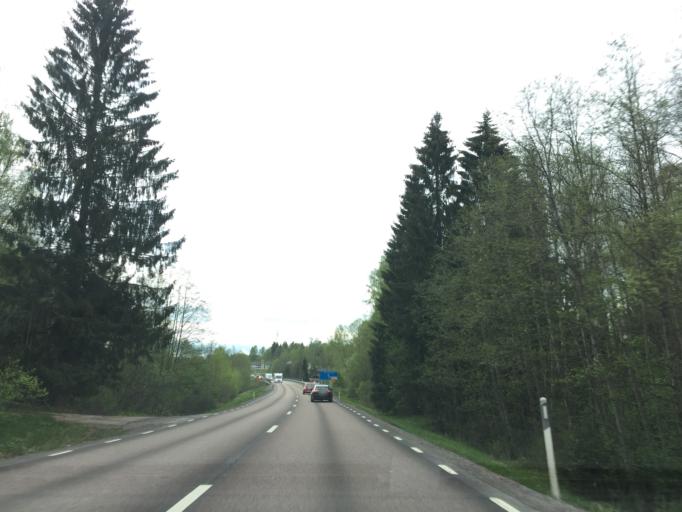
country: SE
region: Vaermland
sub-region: Eda Kommun
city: Charlottenberg
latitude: 59.9166
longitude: 12.2740
